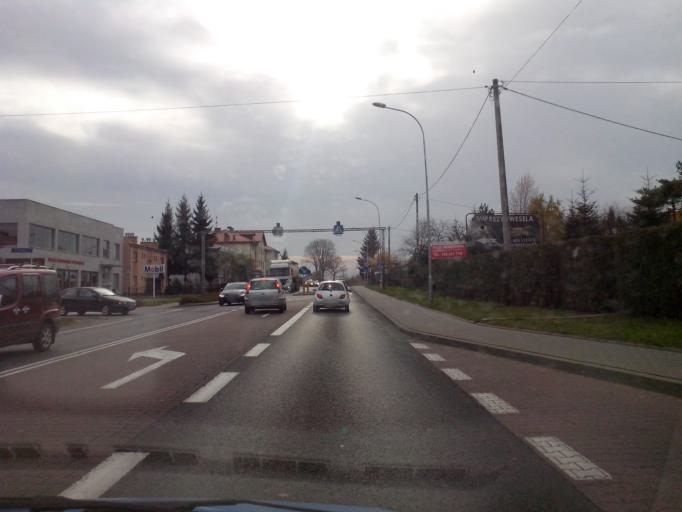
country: PL
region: Subcarpathian Voivodeship
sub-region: Powiat rzeszowski
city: Boguchwala
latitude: 49.9818
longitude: 21.9392
